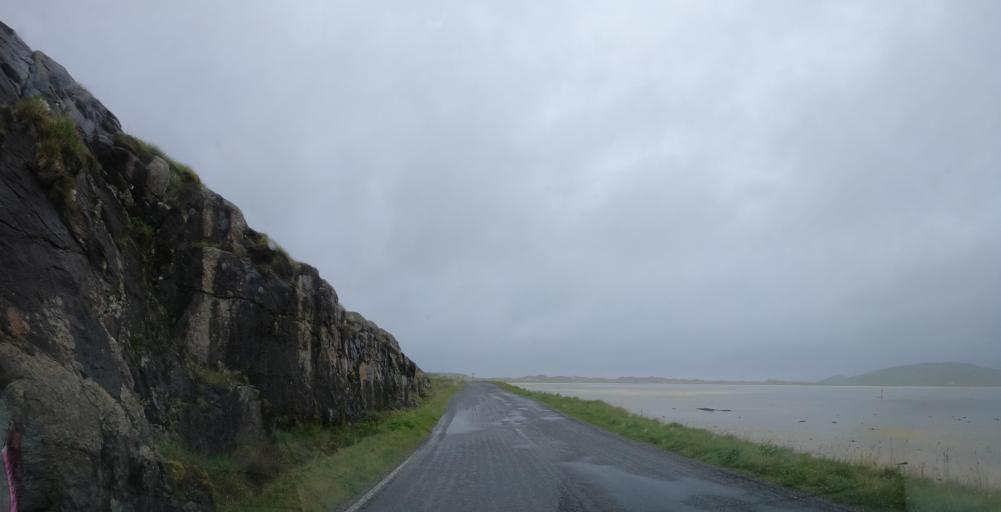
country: GB
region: Scotland
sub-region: Eilean Siar
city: Barra
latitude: 57.0176
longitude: -7.4376
